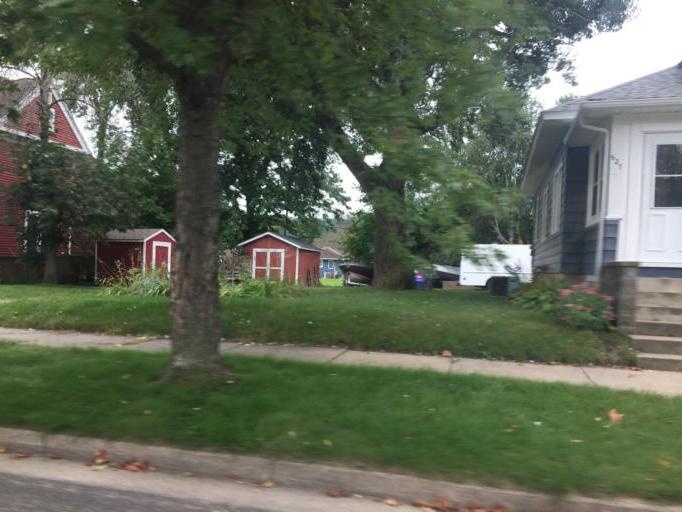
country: US
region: Minnesota
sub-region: Winona County
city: Winona
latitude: 44.0481
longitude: -91.6567
